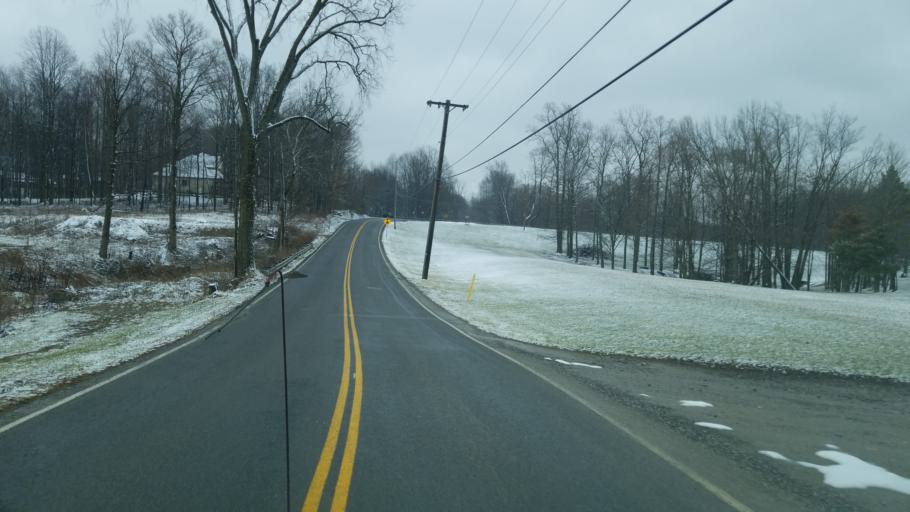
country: US
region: Ohio
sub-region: Portage County
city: Mantua
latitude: 41.2869
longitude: -81.2452
